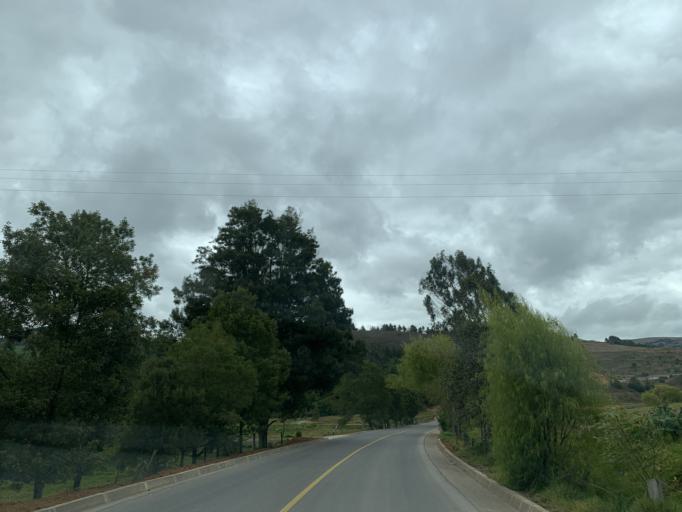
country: CO
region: Boyaca
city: Tunja
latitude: 5.5298
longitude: -73.3292
